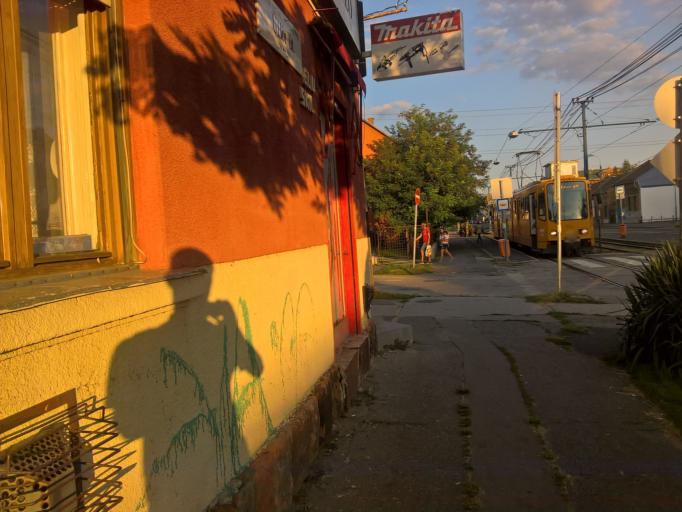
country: HU
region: Budapest
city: Budapest XIX. keruelet
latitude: 47.4500
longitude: 19.1628
